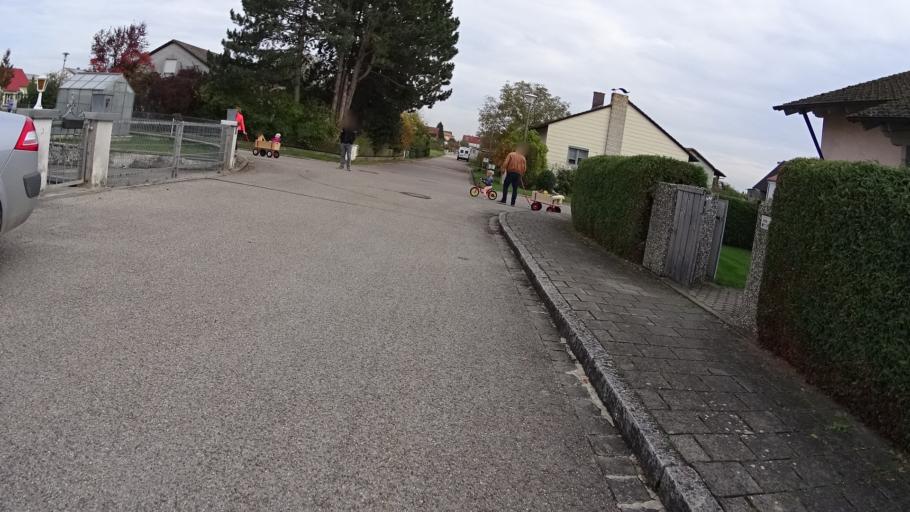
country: DE
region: Bavaria
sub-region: Upper Bavaria
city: Adelschlag
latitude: 48.8639
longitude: 11.2390
